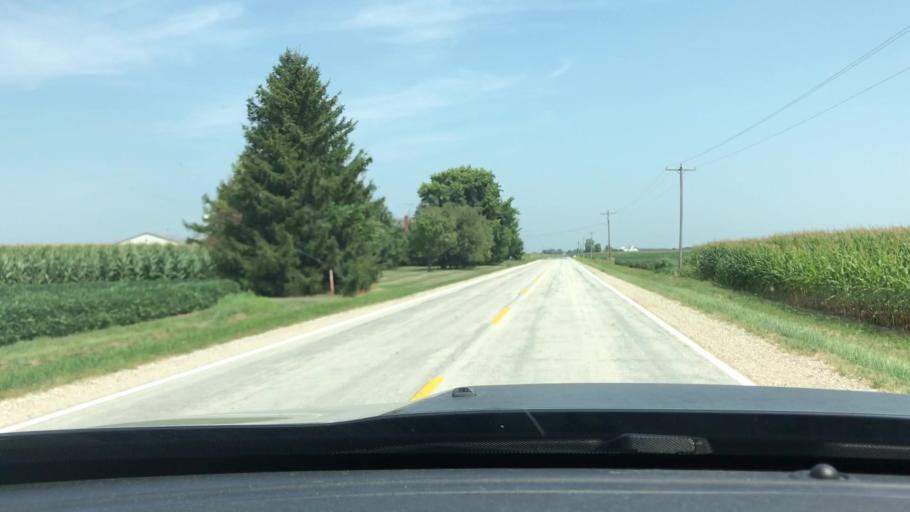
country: US
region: Illinois
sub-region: LaSalle County
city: Sheridan
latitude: 41.4955
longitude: -88.7355
